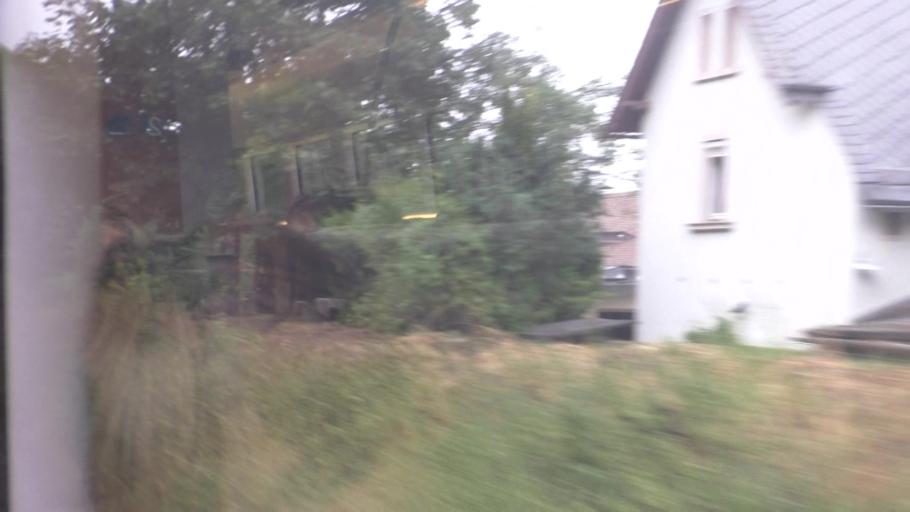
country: DE
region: Saxony
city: Eibau
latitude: 50.9740
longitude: 14.6820
